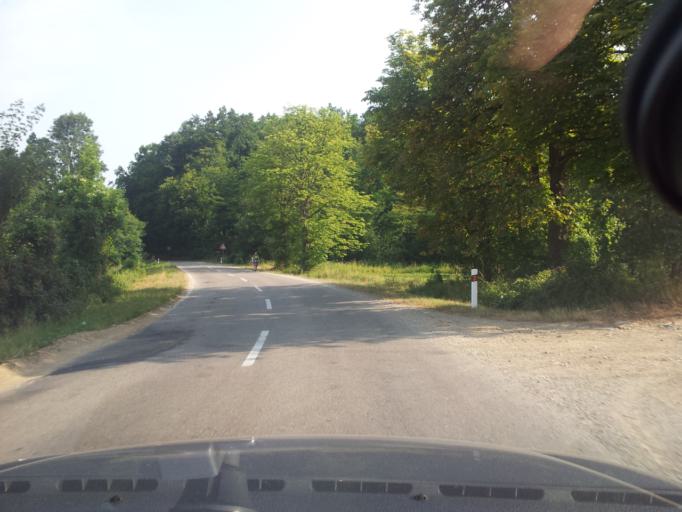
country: SK
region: Nitriansky
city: Trencianske Teplice
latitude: 48.8719
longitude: 18.1869
